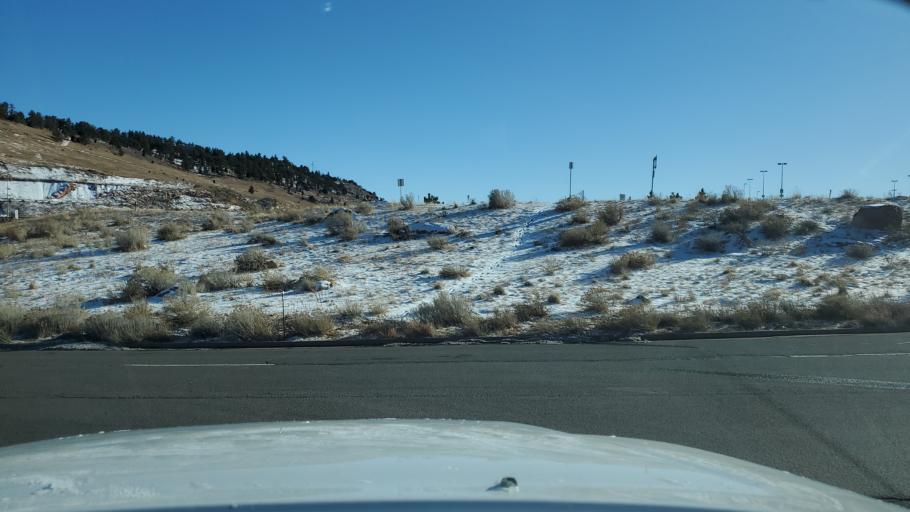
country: US
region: Colorado
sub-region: Jefferson County
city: West Pleasant View
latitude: 39.7018
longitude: -105.2059
